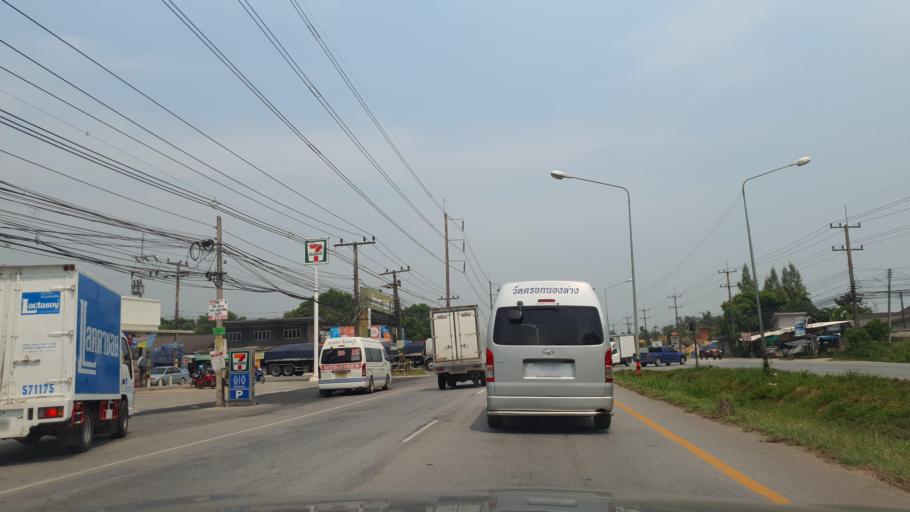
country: TH
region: Rayong
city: Rayong
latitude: 12.6435
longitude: 101.3549
